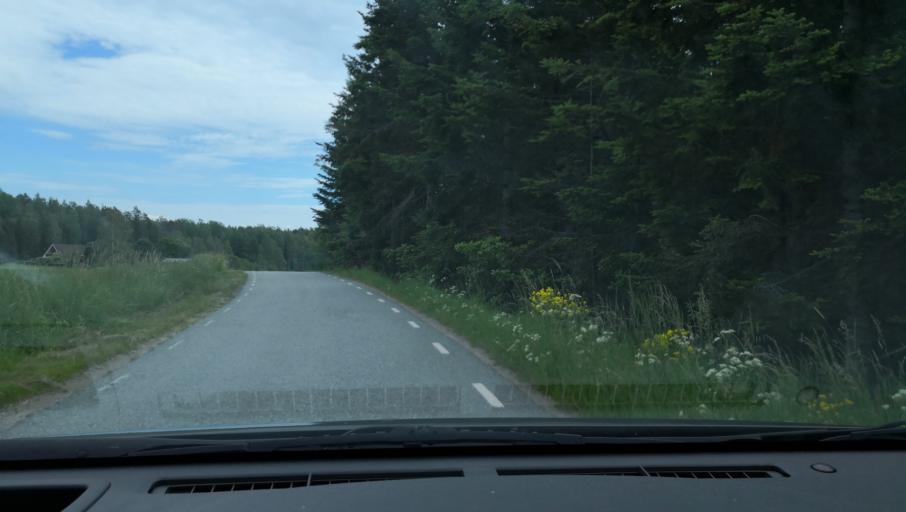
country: SE
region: Uppsala
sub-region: Enkopings Kommun
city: Orsundsbro
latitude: 59.6995
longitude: 17.4309
